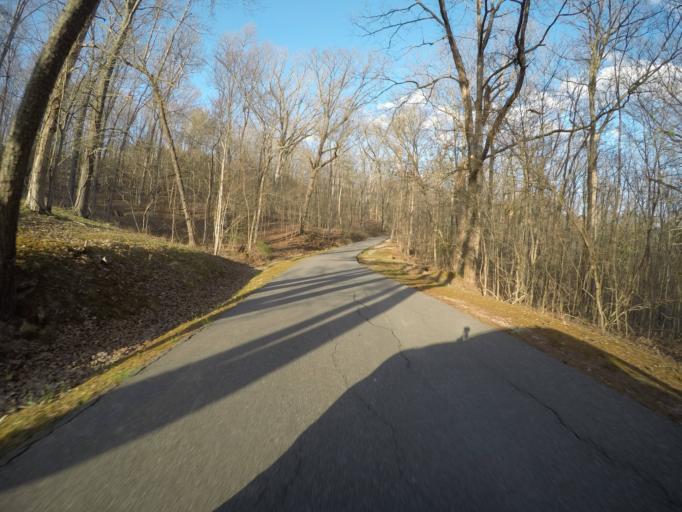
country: US
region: West Virginia
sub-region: Kanawha County
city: Charleston
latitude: 38.3894
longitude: -81.5683
